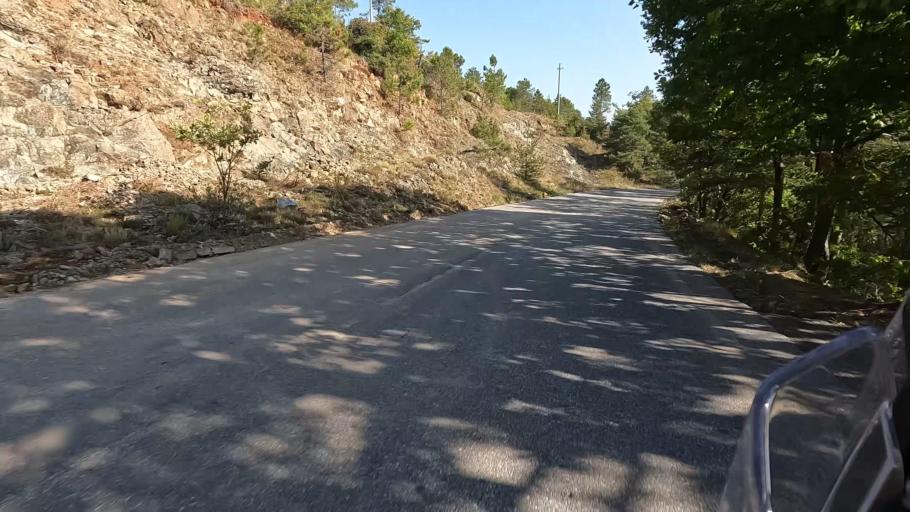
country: IT
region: Liguria
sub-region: Provincia di Savona
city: Urbe
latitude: 44.5026
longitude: 8.5427
